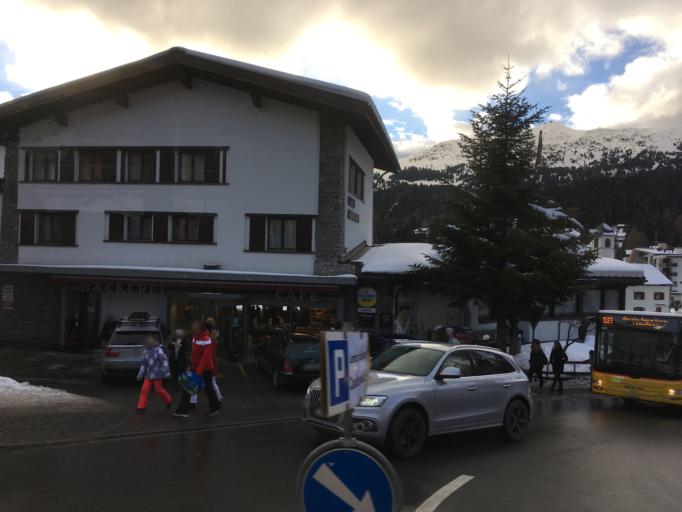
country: CH
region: Grisons
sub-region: Plessur District
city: Churwalden
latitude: 46.7294
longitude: 9.5570
